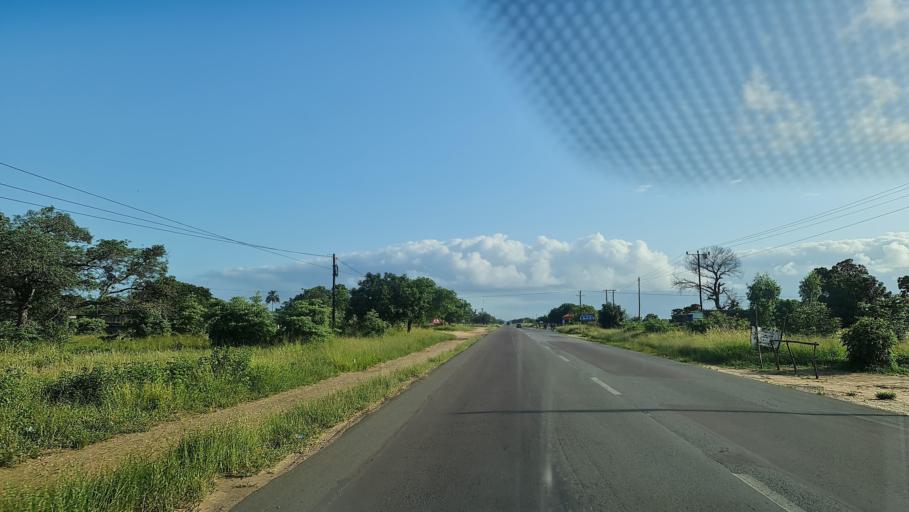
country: MZ
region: Maputo City
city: Maputo
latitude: -25.6847
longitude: 32.6655
